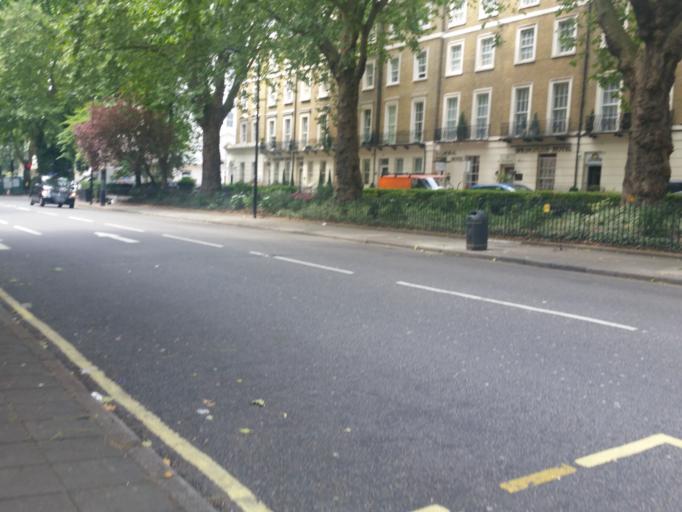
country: GB
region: England
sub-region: Greater London
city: Bayswater
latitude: 51.5153
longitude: -0.1724
